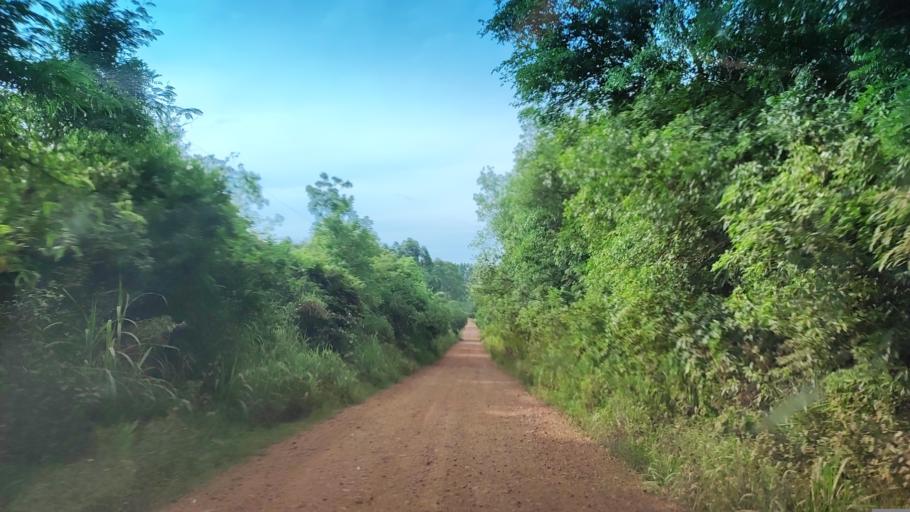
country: AR
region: Misiones
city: Gobernador Roca
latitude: -27.1673
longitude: -55.5125
